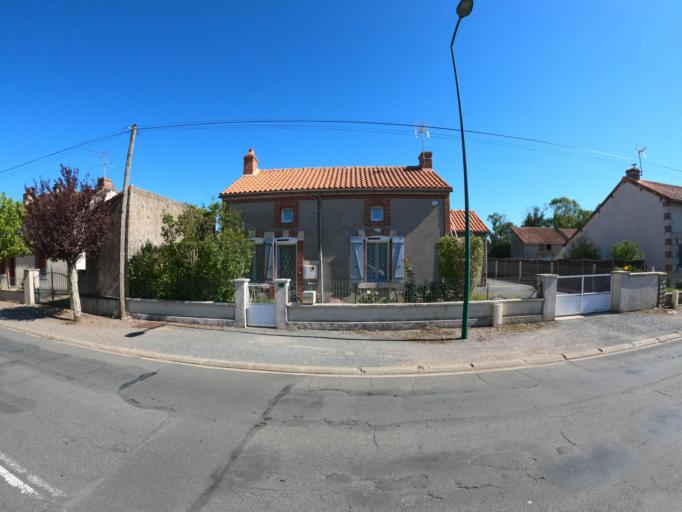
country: FR
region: Poitou-Charentes
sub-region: Departement de la Vienne
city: Lathus-Saint-Remy
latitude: 46.3368
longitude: 0.9564
